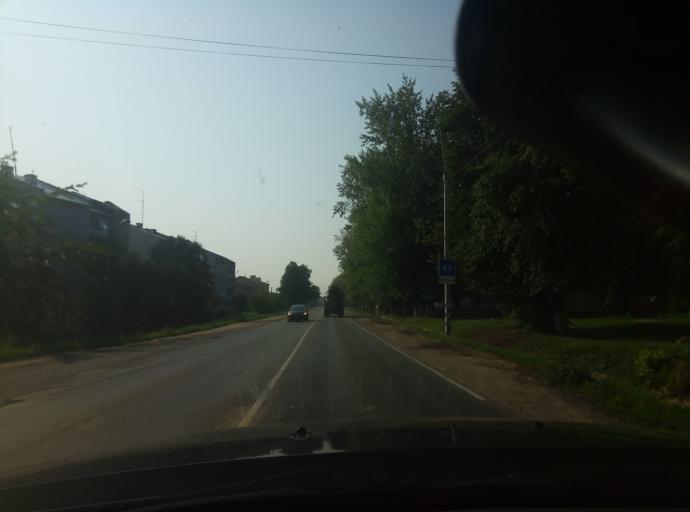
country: RU
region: Kaluga
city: Belousovo
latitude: 55.0921
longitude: 36.6653
